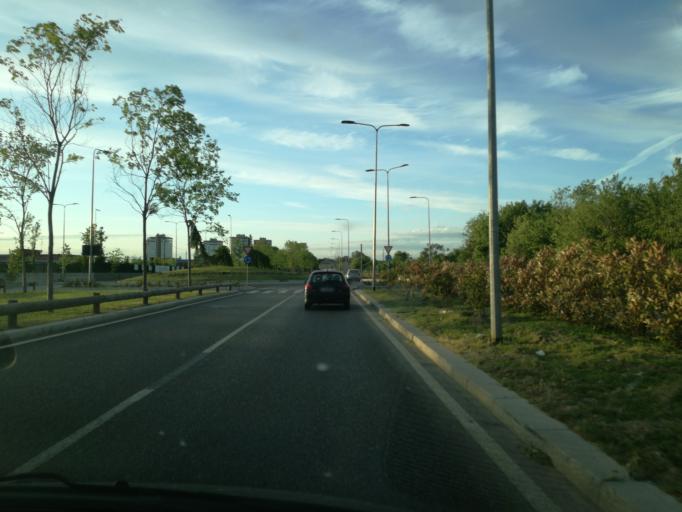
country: IT
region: Lombardy
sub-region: Citta metropolitana di Milano
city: Noverasco-Sporting Mirasole
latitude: 45.4155
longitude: 9.2060
